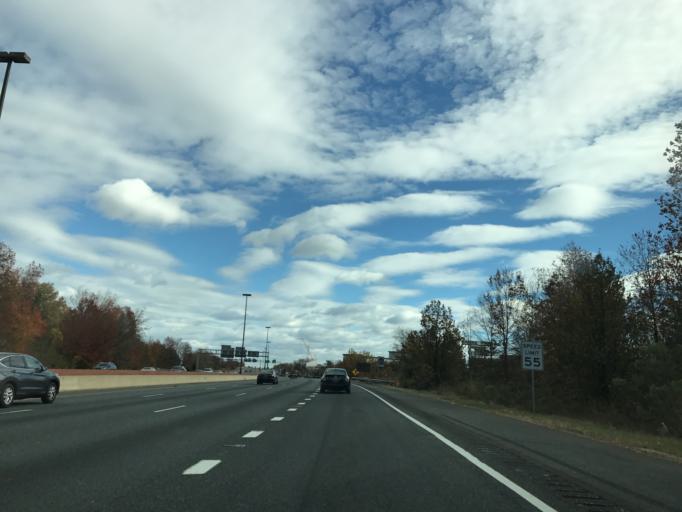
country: US
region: Maryland
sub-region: Anne Arundel County
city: Parole
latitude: 38.9823
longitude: -76.5528
